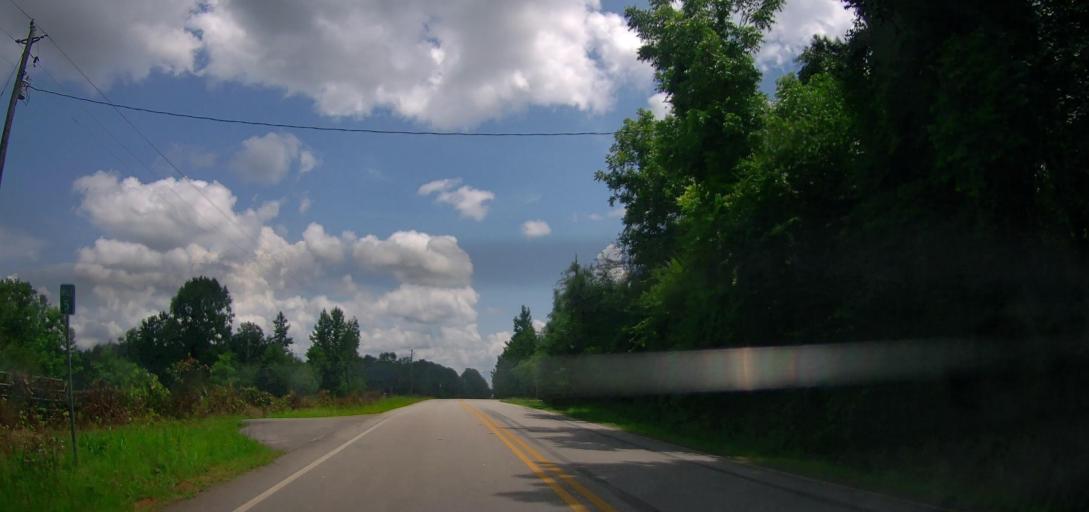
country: US
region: Georgia
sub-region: Meriwether County
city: Greenville
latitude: 33.0759
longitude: -84.7731
